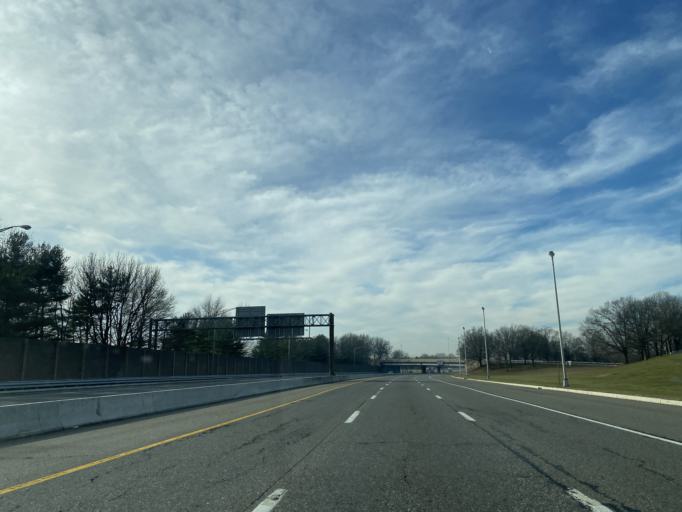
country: US
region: New Jersey
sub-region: Burlington County
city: Palmyra
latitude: 39.9744
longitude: -75.0288
